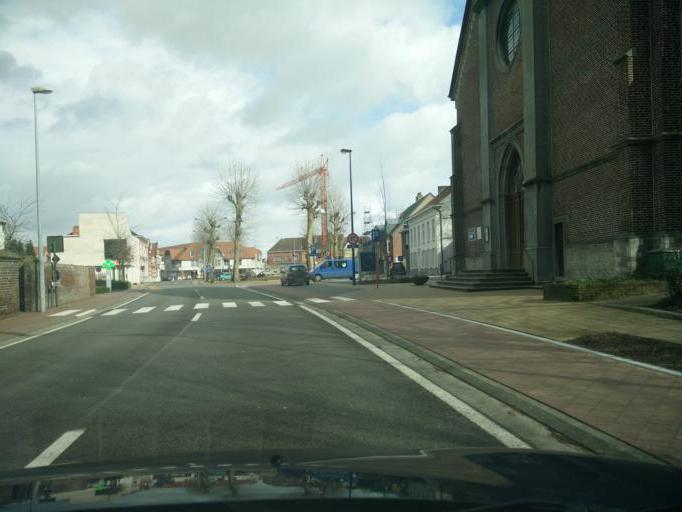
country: BE
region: Flanders
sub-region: Provincie Oost-Vlaanderen
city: Melle
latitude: 51.0282
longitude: 3.7988
